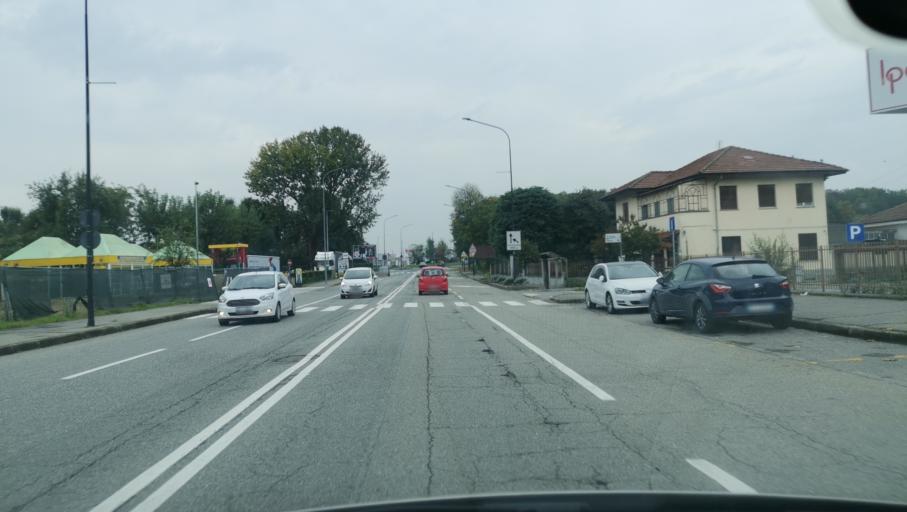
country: IT
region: Piedmont
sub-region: Provincia di Torino
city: Settimo Torinese
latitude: 45.1277
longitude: 7.7526
